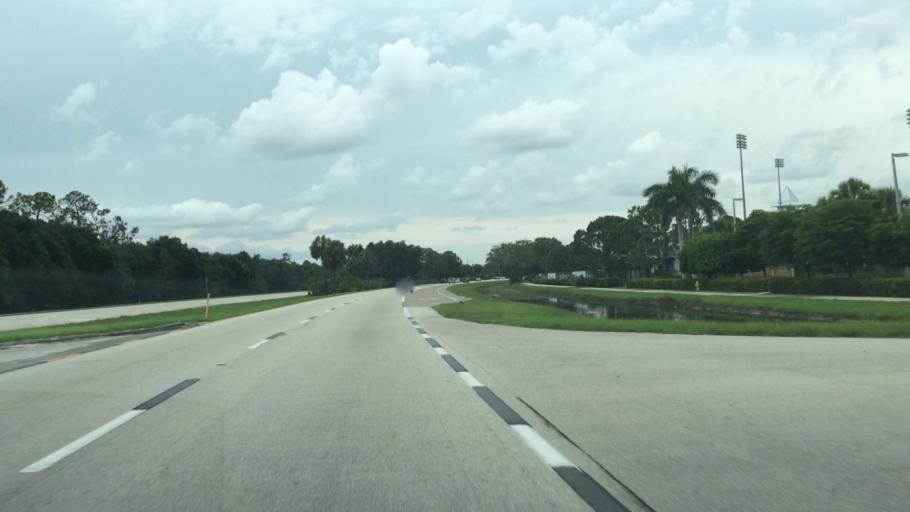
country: US
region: Florida
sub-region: Lee County
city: Villas
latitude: 26.5399
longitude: -81.8399
